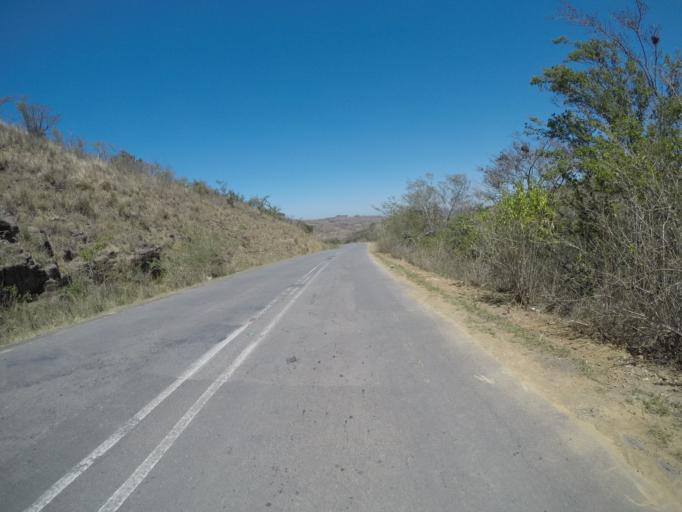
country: ZA
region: Eastern Cape
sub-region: OR Tambo District Municipality
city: Mthatha
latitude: -31.9123
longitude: 28.9610
